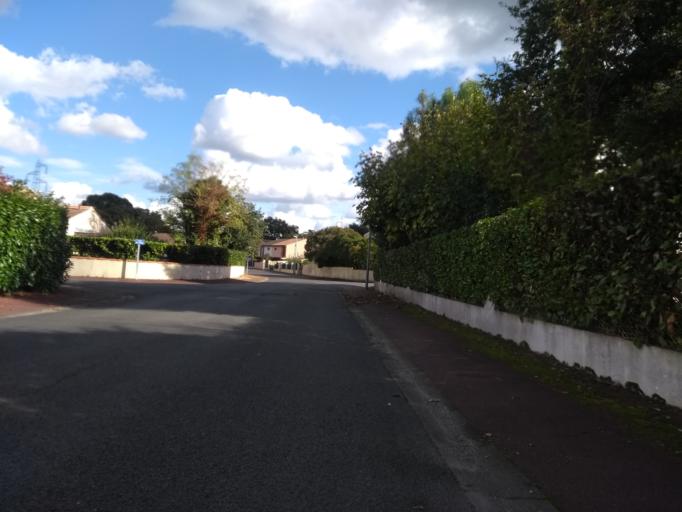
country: FR
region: Aquitaine
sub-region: Departement de la Gironde
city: Canejan
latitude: 44.7585
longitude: -0.6413
